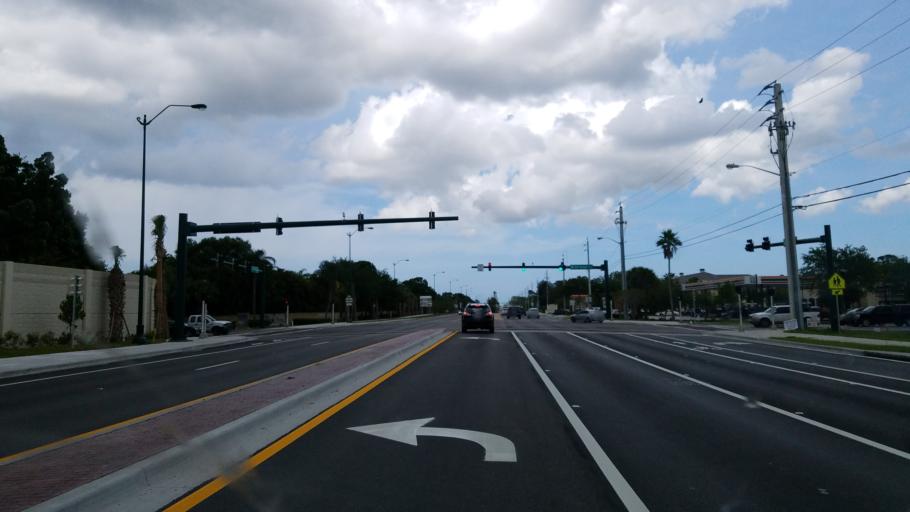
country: US
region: Florida
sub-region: Martin County
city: Palm City
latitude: 27.1614
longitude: -80.2970
